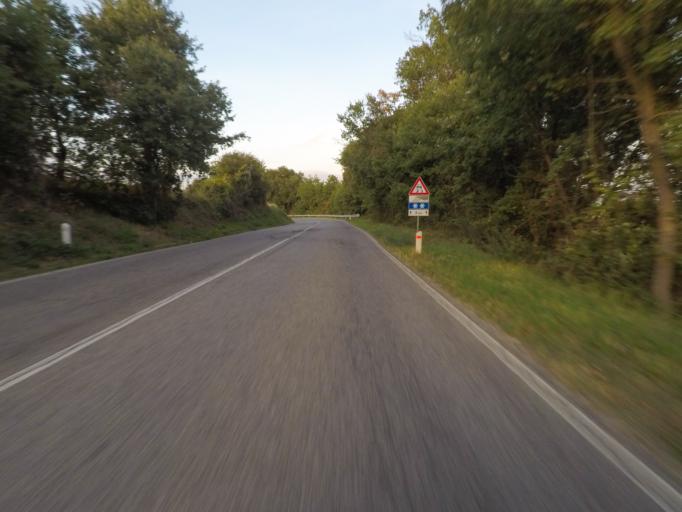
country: IT
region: Tuscany
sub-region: Provincia di Siena
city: Torrita di Siena
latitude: 43.1398
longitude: 11.7365
